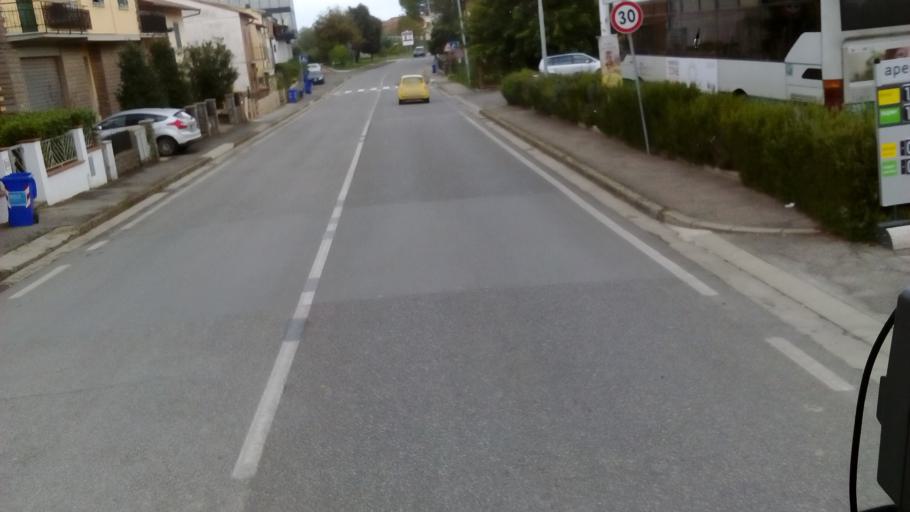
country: IT
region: Tuscany
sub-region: Province of Florence
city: Montespertoli
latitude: 43.6460
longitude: 11.0655
